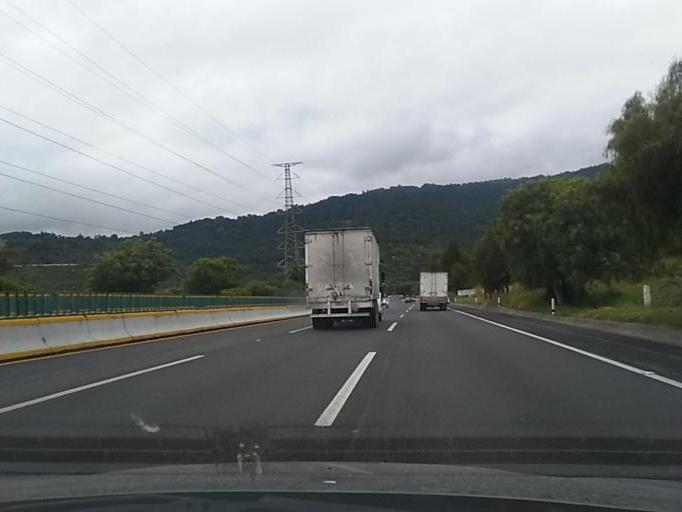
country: MX
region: Mexico City
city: Xochimilco
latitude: 19.2330
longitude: -99.1439
